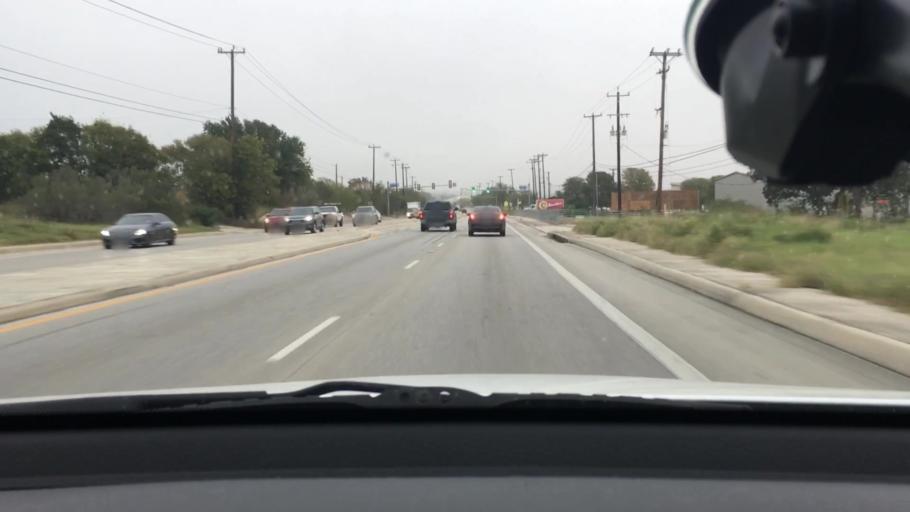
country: US
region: Texas
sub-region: Bexar County
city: Live Oak
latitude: 29.5945
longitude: -98.3463
